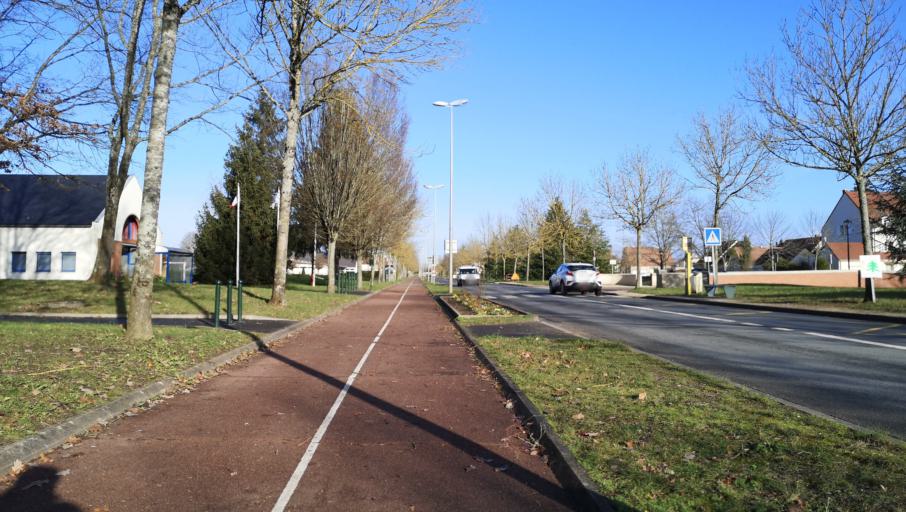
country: FR
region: Centre
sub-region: Departement du Loiret
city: Saint-Jean-le-Blanc
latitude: 47.8872
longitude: 1.9285
